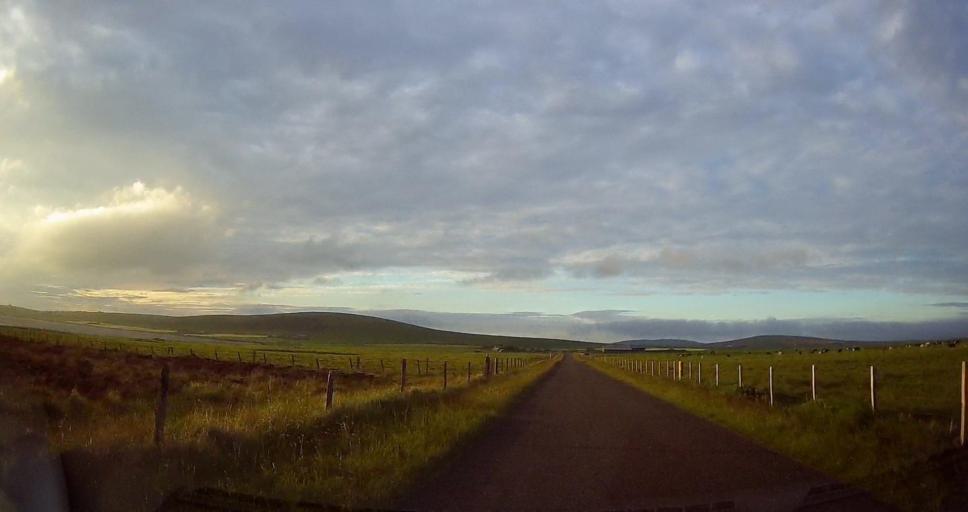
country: GB
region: Scotland
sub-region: Orkney Islands
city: Stromness
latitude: 59.1042
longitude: -3.2572
